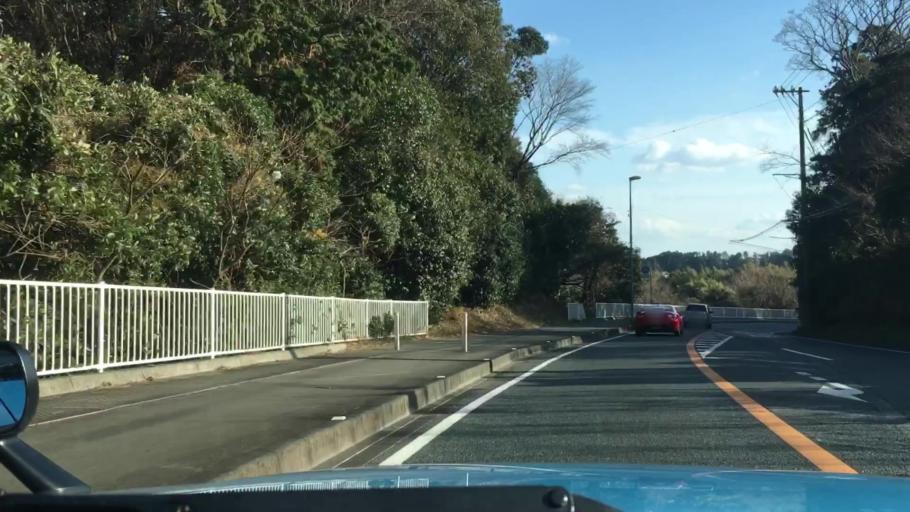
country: JP
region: Shizuoka
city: Hamamatsu
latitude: 34.7515
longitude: 137.6730
